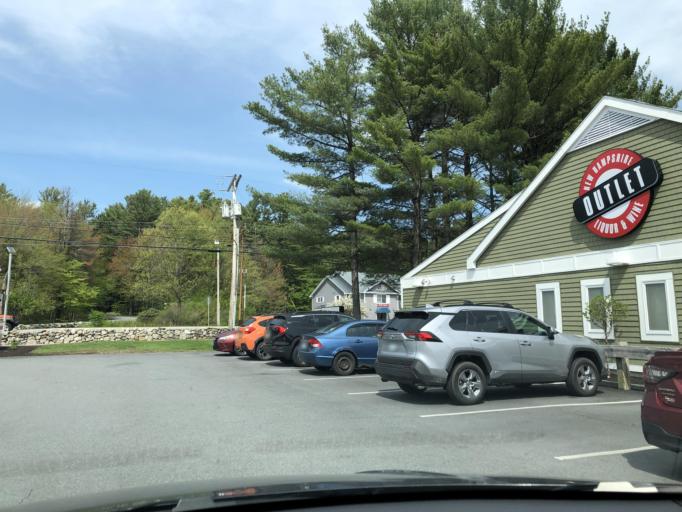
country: US
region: New Hampshire
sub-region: Merrimack County
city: New London
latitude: 43.4232
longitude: -72.0026
